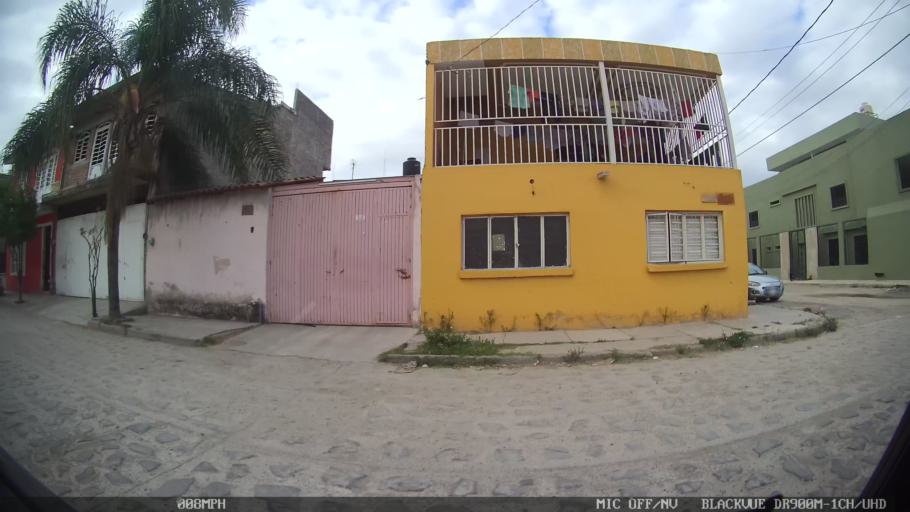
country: MX
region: Jalisco
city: Tonala
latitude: 20.6655
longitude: -103.2382
